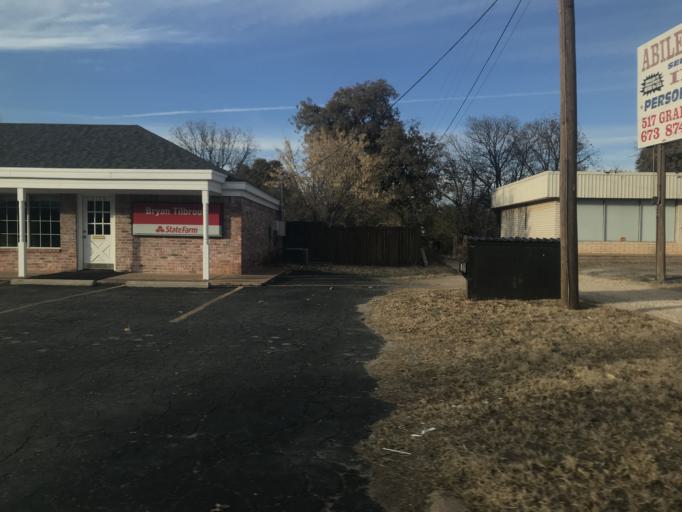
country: US
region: Texas
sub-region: Taylor County
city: Abilene
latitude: 32.4323
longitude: -99.7609
